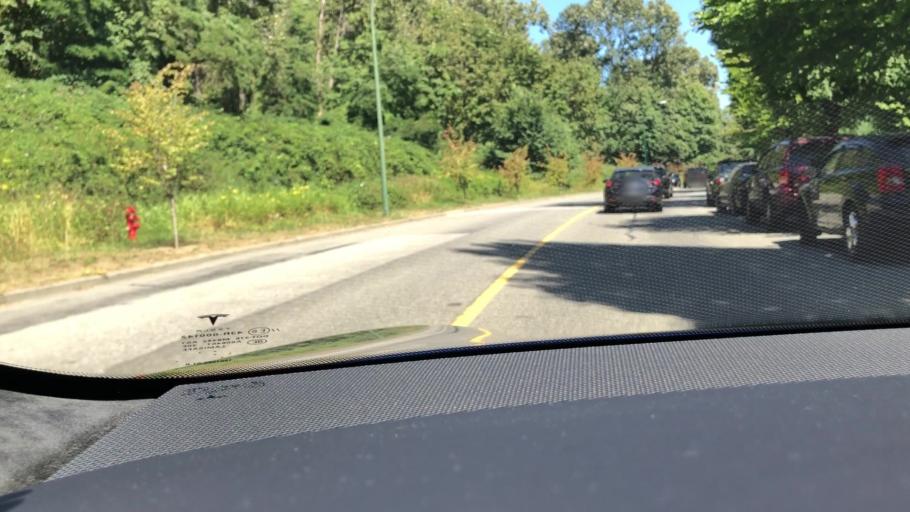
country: CA
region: British Columbia
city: Vancouver
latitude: 49.2086
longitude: -123.0343
